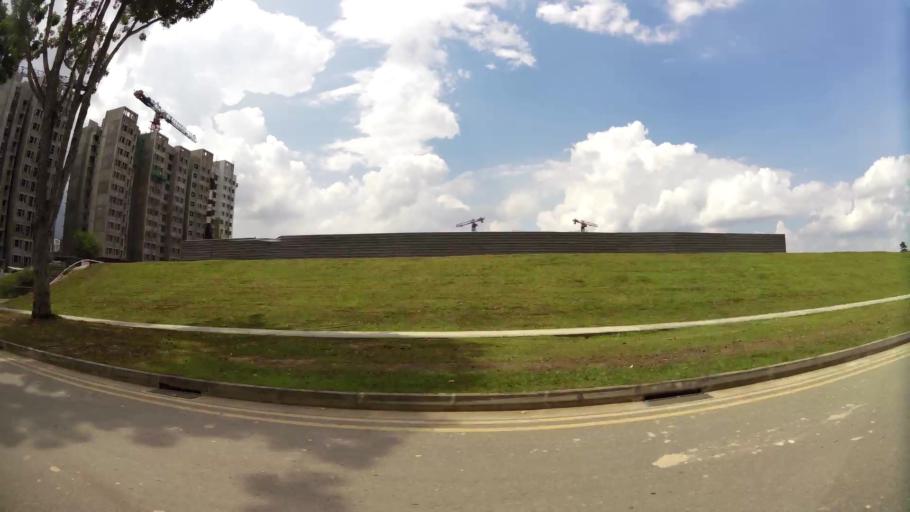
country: MY
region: Johor
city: Kampung Pasir Gudang Baru
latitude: 1.4255
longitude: 103.8534
